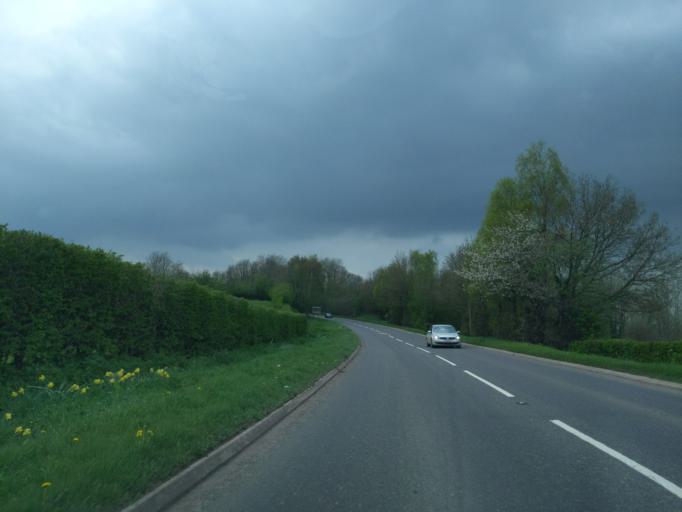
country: GB
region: England
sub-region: Devon
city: Crediton
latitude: 50.7797
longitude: -3.6154
